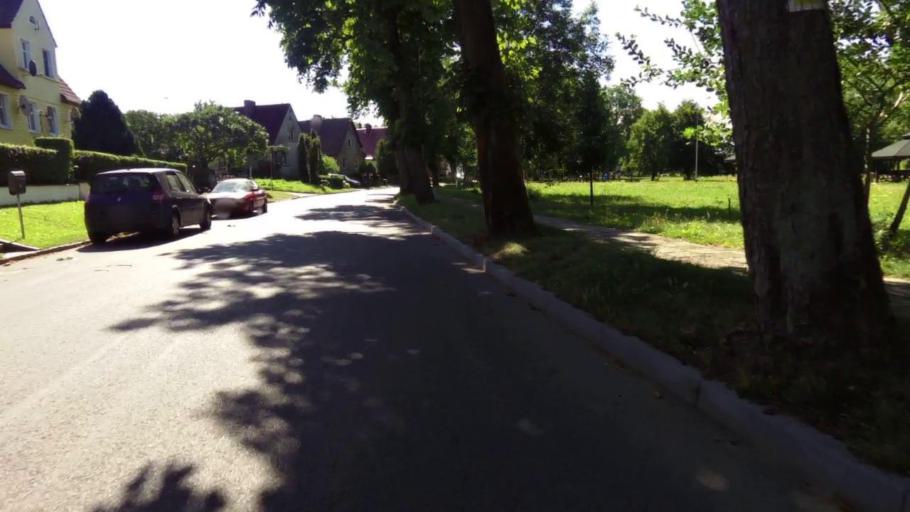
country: PL
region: West Pomeranian Voivodeship
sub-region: Powiat drawski
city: Zlocieniec
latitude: 53.5410
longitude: 16.0029
